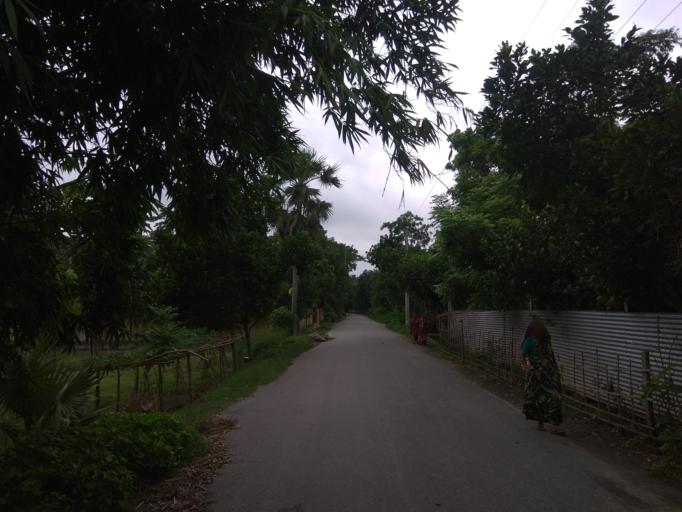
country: BD
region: Dhaka
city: Dohar
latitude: 23.4488
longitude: 90.0615
